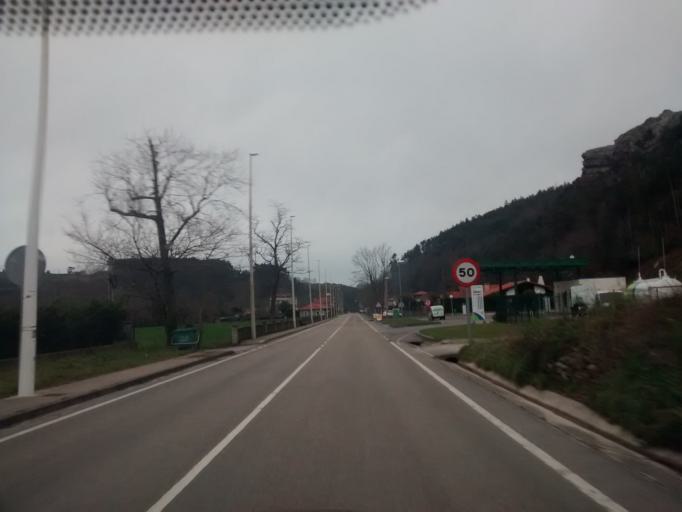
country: ES
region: Cantabria
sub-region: Provincia de Cantabria
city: Entrambasaguas
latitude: 43.3570
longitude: -3.7098
